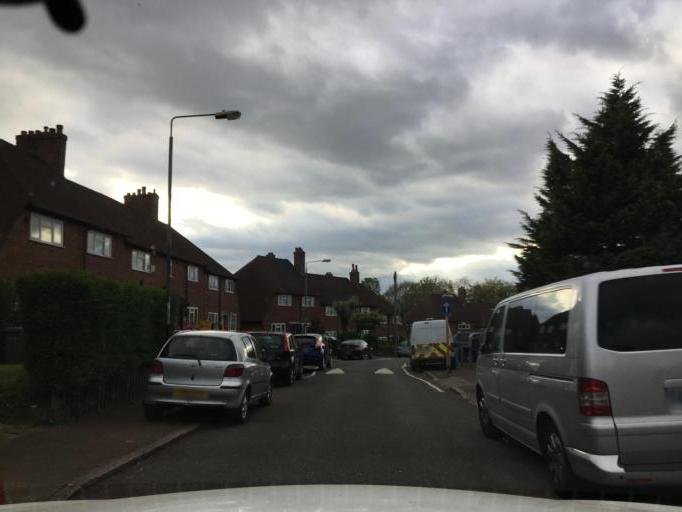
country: GB
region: England
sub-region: Greater London
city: Blackheath
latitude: 51.4446
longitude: 0.0368
